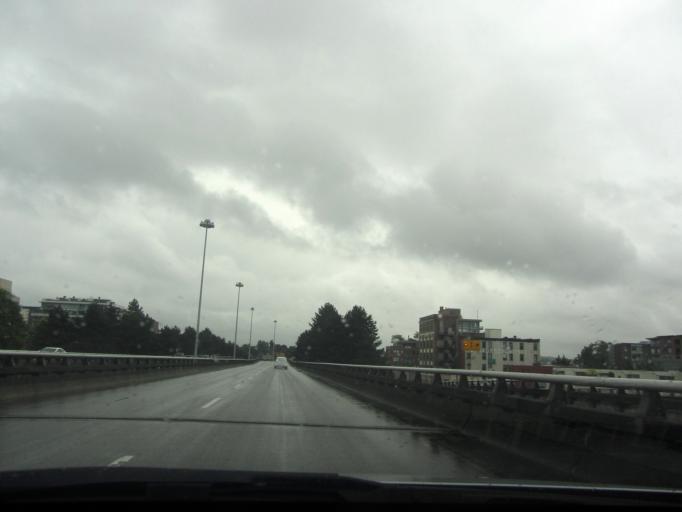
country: CA
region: British Columbia
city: West End
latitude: 49.2771
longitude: -123.1024
